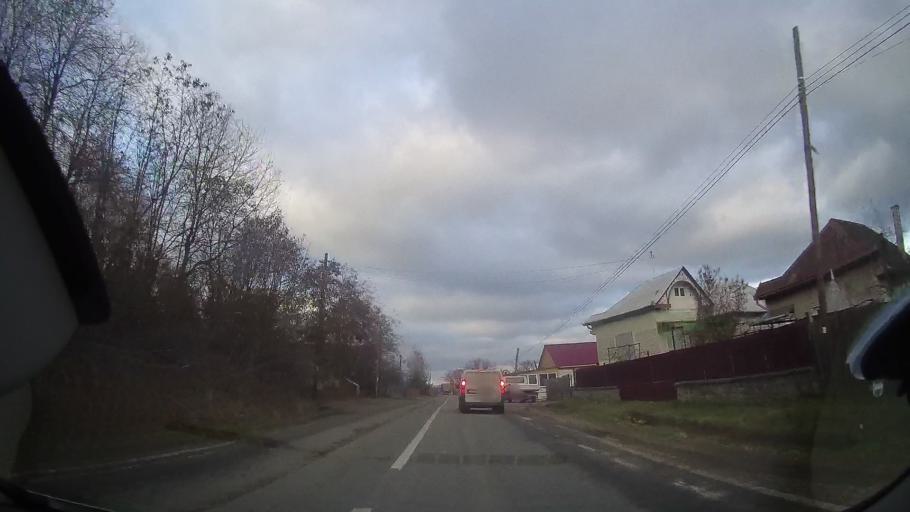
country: RO
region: Cluj
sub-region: Comuna Sancraiu
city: Sancraiu
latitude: 46.8017
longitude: 22.9949
